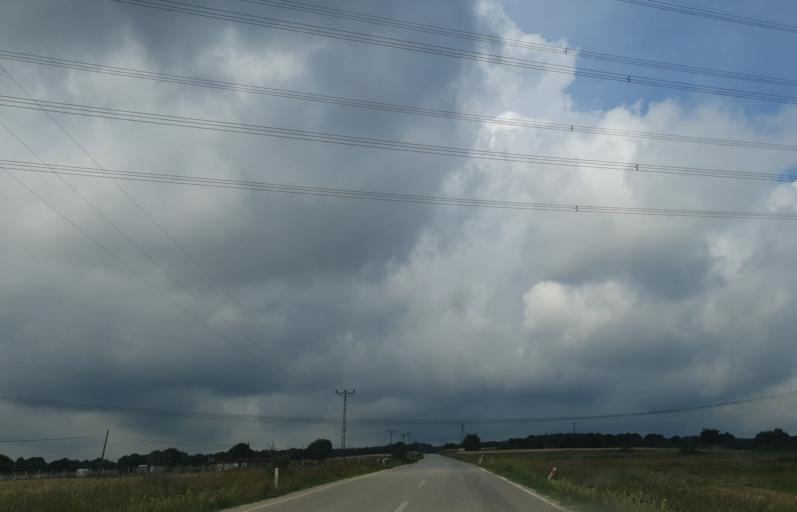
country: TR
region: Tekirdag
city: Saray
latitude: 41.4819
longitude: 27.9616
